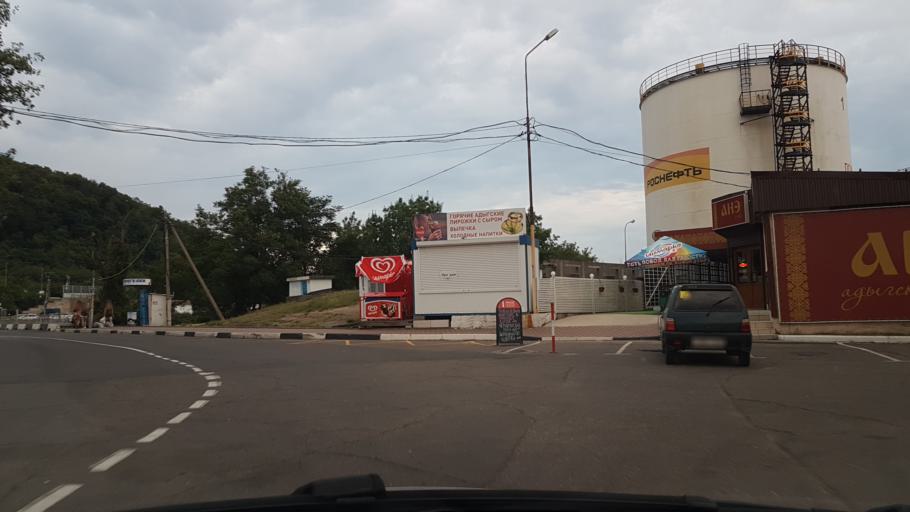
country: RU
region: Krasnodarskiy
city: Tuapse
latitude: 44.0908
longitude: 39.0813
